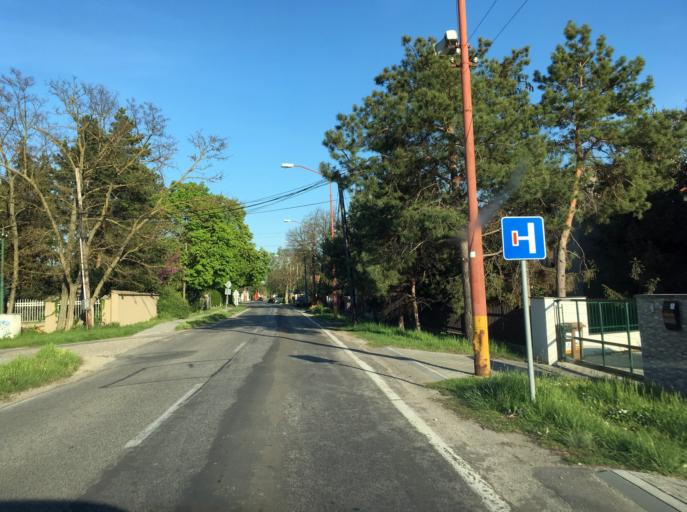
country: AT
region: Burgenland
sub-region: Politischer Bezirk Neusiedl am See
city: Deutsch Jahrndorf
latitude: 48.0578
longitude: 17.1391
